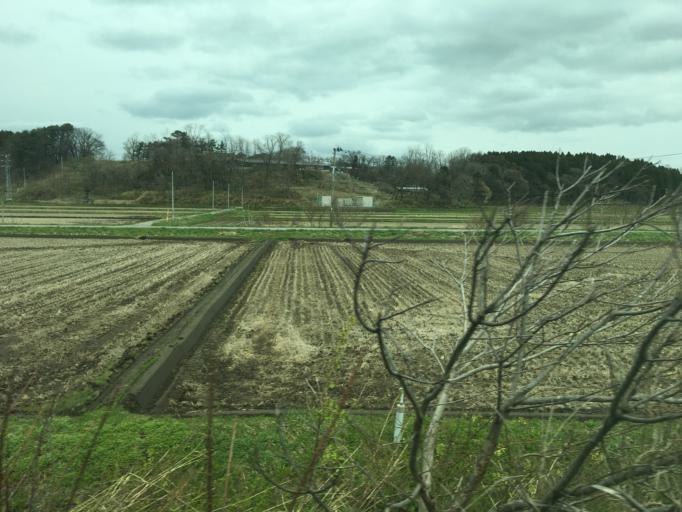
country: JP
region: Aomori
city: Shimokizukuri
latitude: 40.7838
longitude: 140.2580
